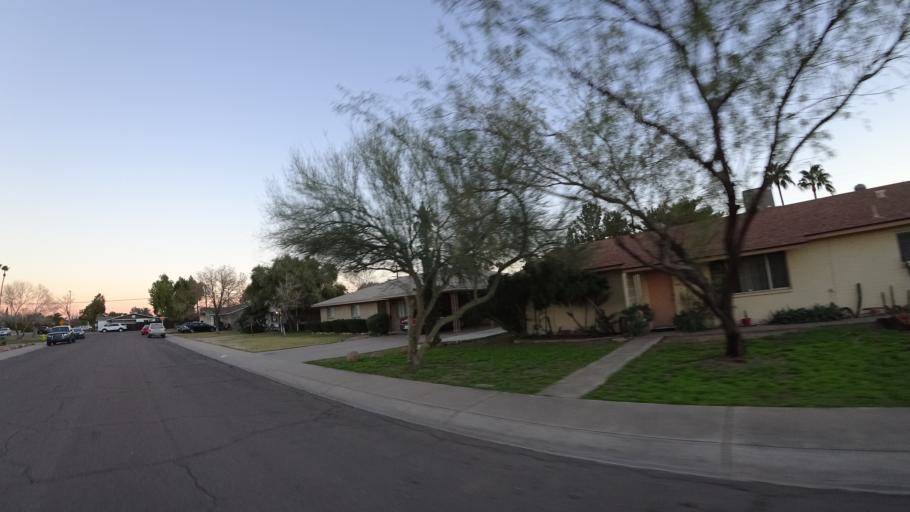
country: US
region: Arizona
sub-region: Maricopa County
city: Tempe Junction
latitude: 33.4188
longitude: -111.9574
